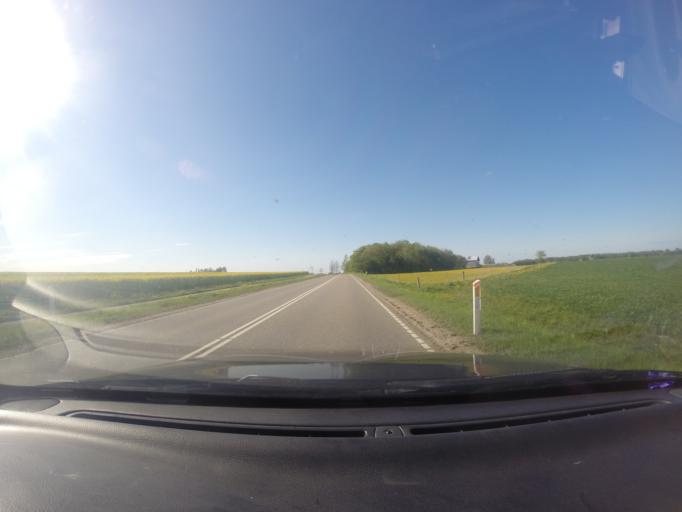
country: DK
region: Capital Region
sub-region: Hoje-Taastrup Kommune
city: Taastrup
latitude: 55.6734
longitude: 12.2721
